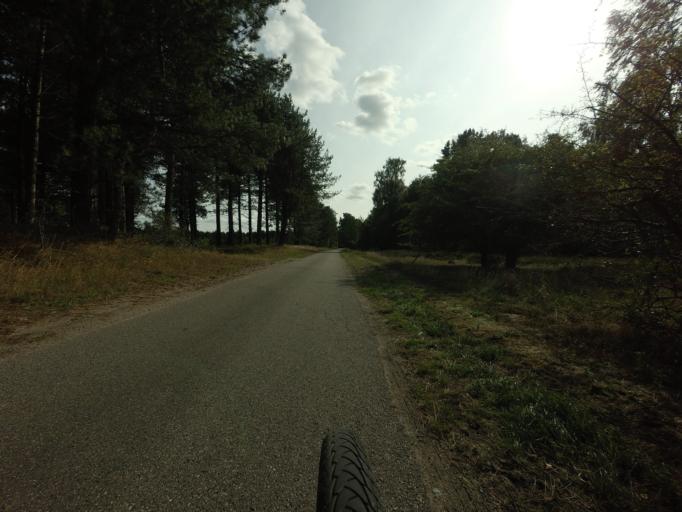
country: DK
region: Zealand
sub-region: Vordingborg Kommune
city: Praesto
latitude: 55.1666
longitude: 12.0950
